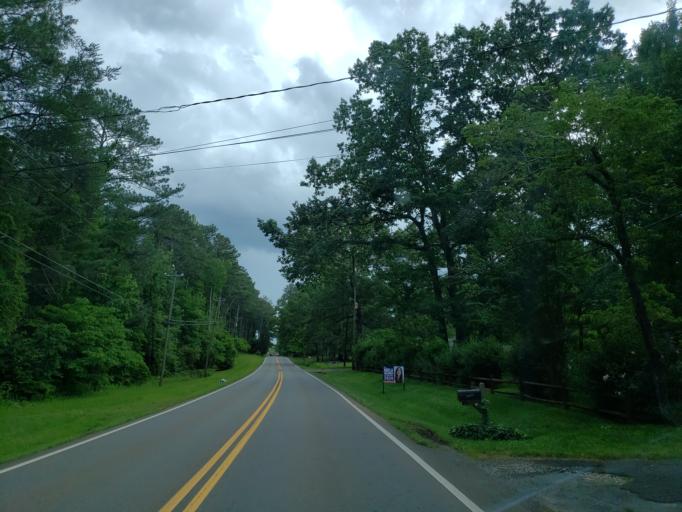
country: US
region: Georgia
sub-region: Pickens County
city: Jasper
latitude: 34.4501
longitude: -84.4239
